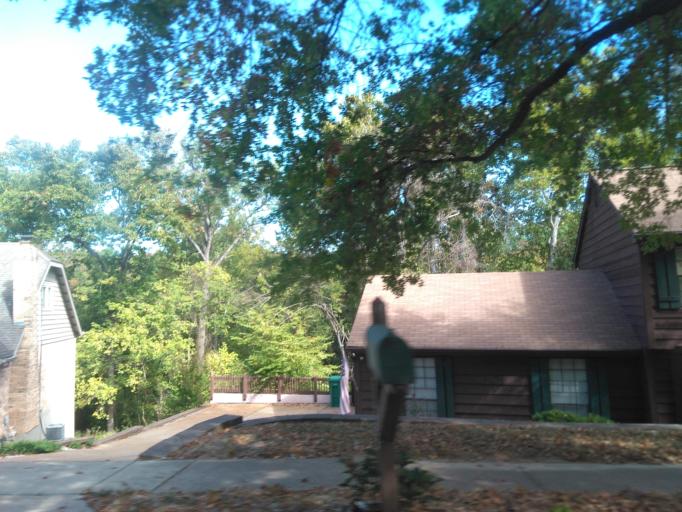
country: US
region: Missouri
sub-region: Saint Louis County
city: Concord
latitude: 38.4834
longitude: -90.3731
